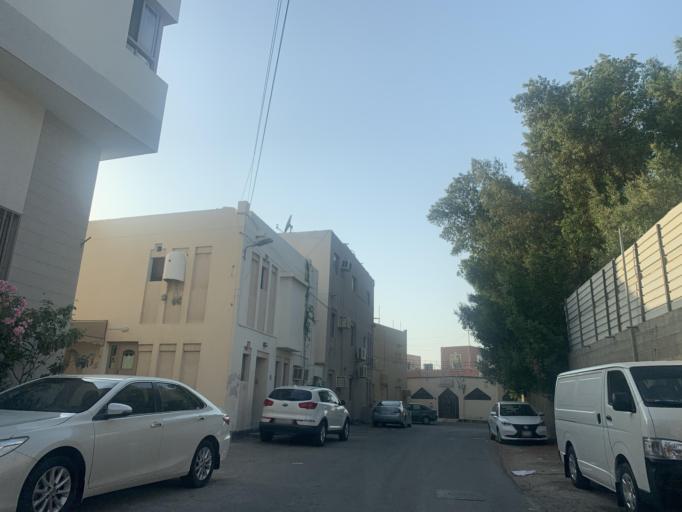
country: BH
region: Manama
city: Jidd Hafs
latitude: 26.2154
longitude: 50.5299
